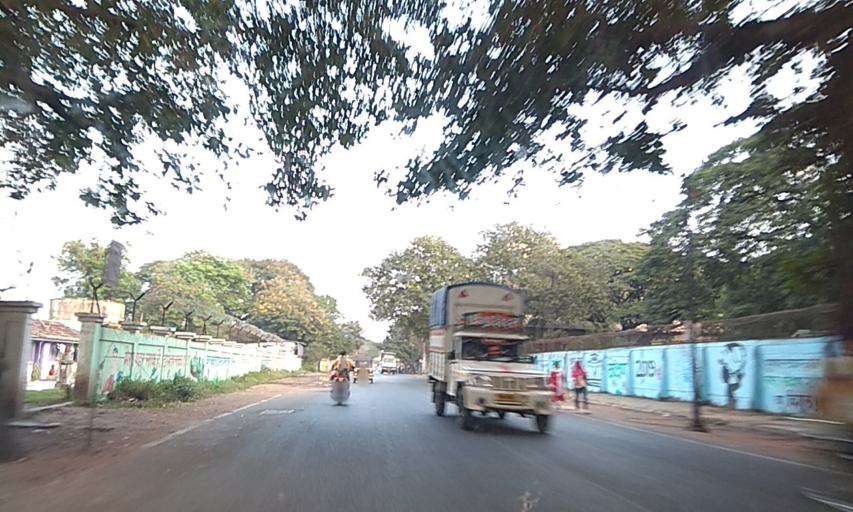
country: IN
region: Maharashtra
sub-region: Pune Division
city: Khadki
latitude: 18.5647
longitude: 73.8819
